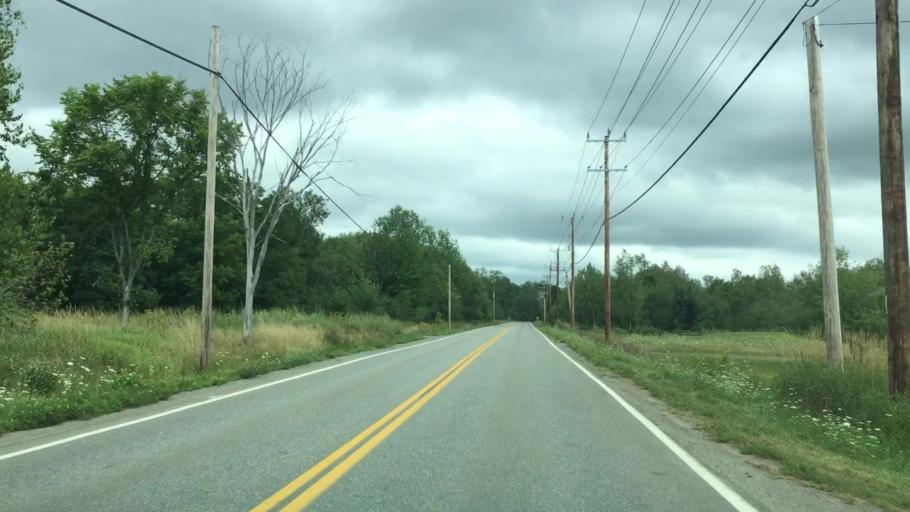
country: US
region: Maine
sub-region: Penobscot County
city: Brewer
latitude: 44.7675
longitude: -68.7622
